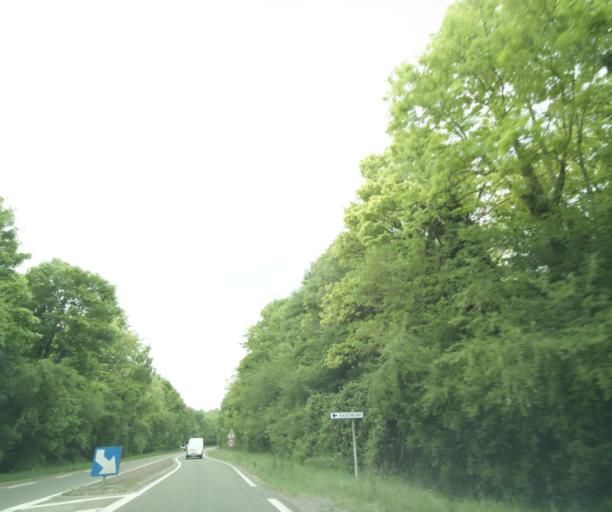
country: FR
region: Ile-de-France
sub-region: Departement des Yvelines
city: Flins-sur-Seine
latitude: 48.9600
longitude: 1.8746
